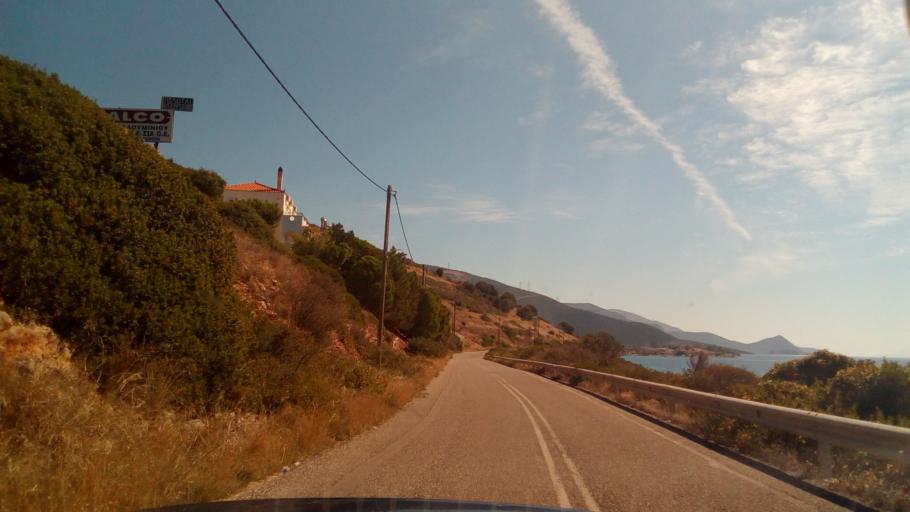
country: GR
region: West Greece
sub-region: Nomos Achaias
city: Selianitika
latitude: 38.3816
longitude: 22.0675
